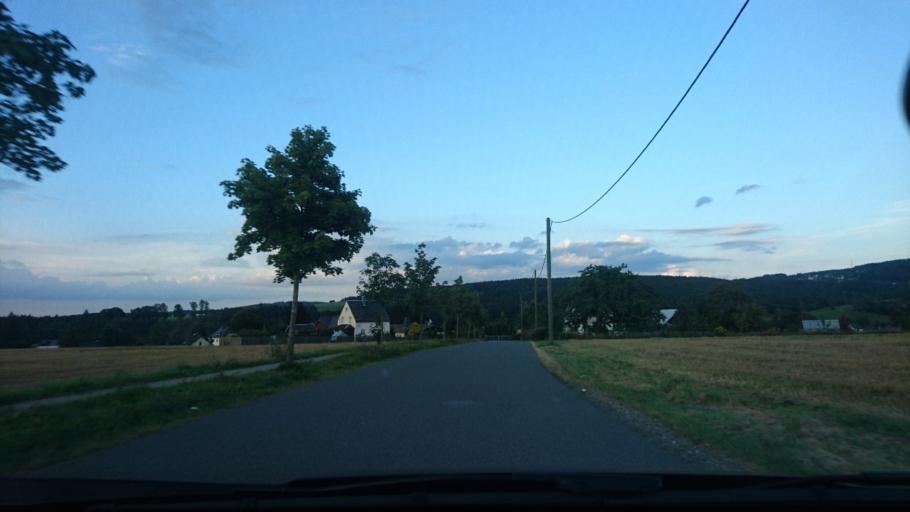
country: DE
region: Saxony
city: Auerbach
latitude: 50.5060
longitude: 12.4201
